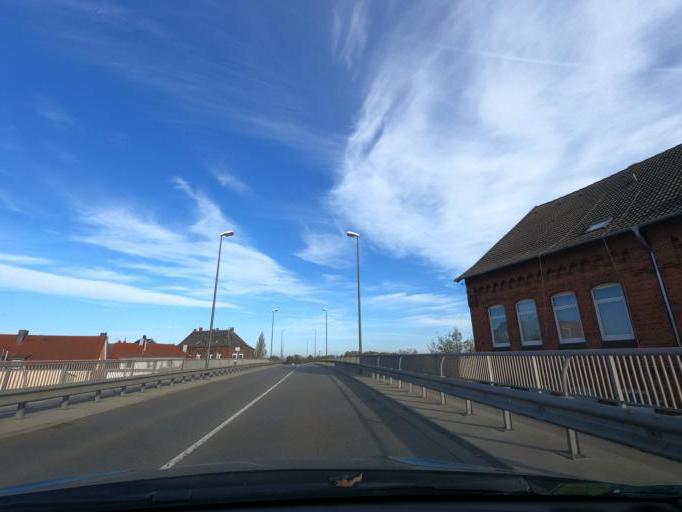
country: DE
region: Lower Saxony
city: Peine
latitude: 52.3177
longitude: 10.2340
